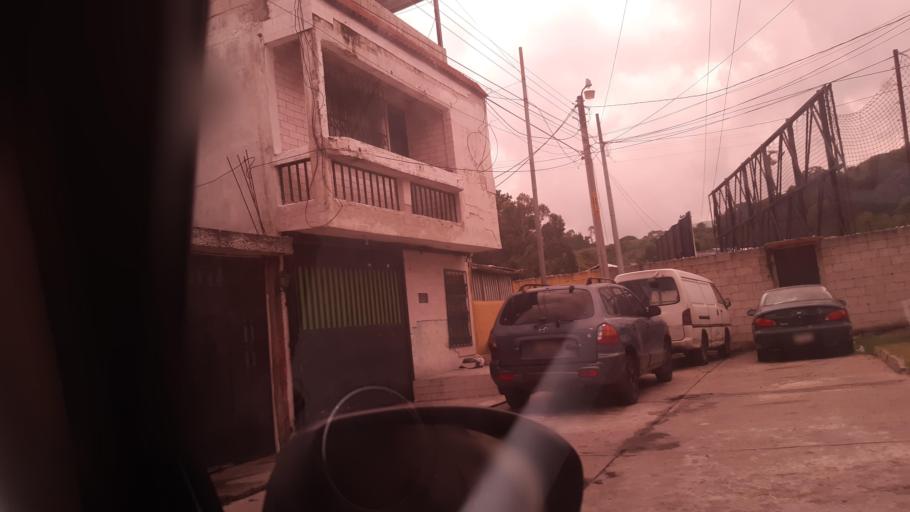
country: GT
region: Guatemala
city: Petapa
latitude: 14.5050
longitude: -90.5438
